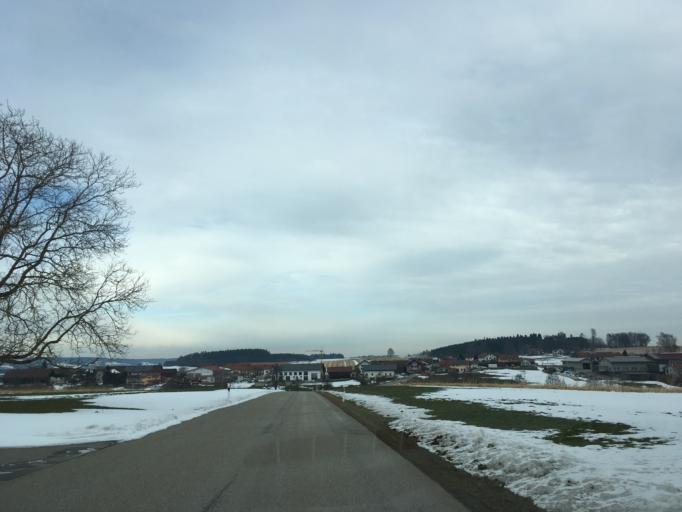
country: DE
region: Bavaria
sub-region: Upper Bavaria
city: Jettenbach
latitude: 48.1227
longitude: 12.3832
